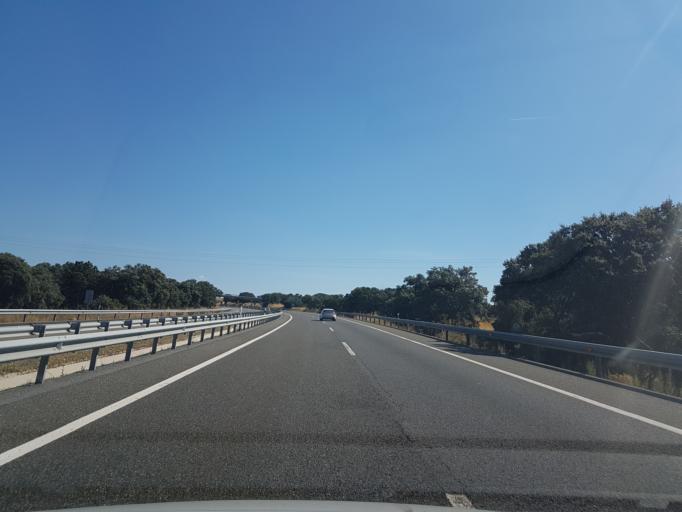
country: ES
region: Castille and Leon
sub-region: Provincia de Avila
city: Avila
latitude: 40.6736
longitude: -4.6794
